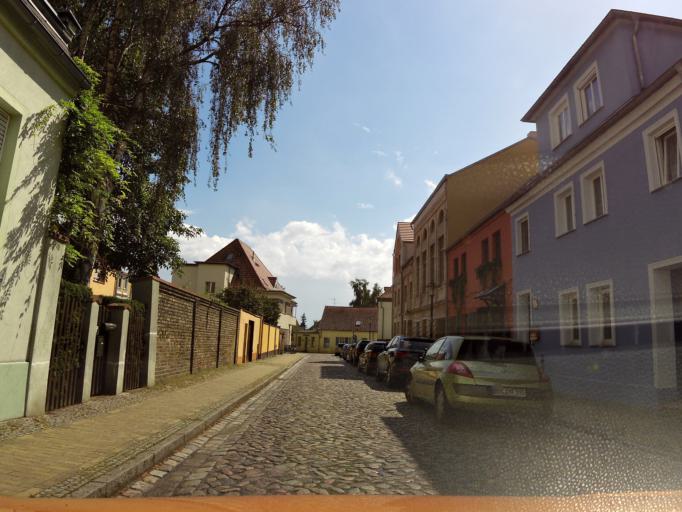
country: DE
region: Brandenburg
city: Ketzin
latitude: 52.4760
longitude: 12.8437
